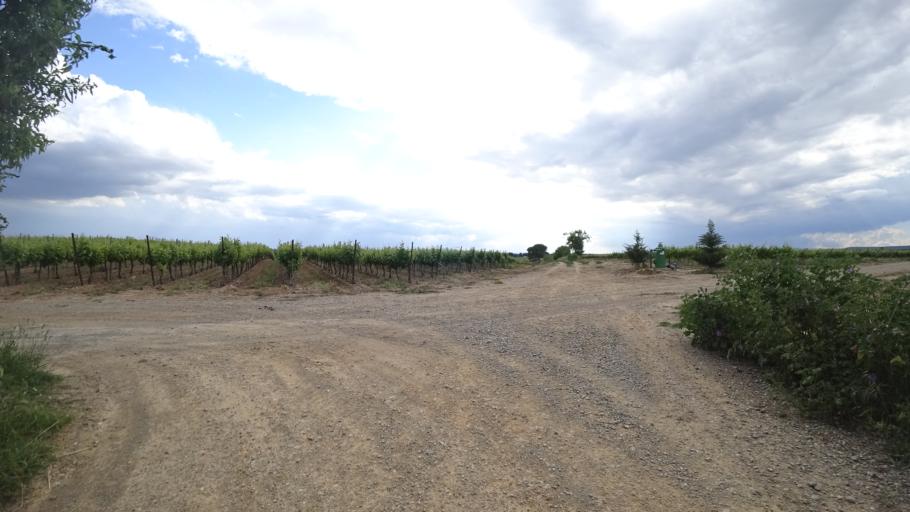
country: FR
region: Languedoc-Roussillon
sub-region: Departement de l'Aude
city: Ginestas
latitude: 43.2534
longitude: 2.8762
